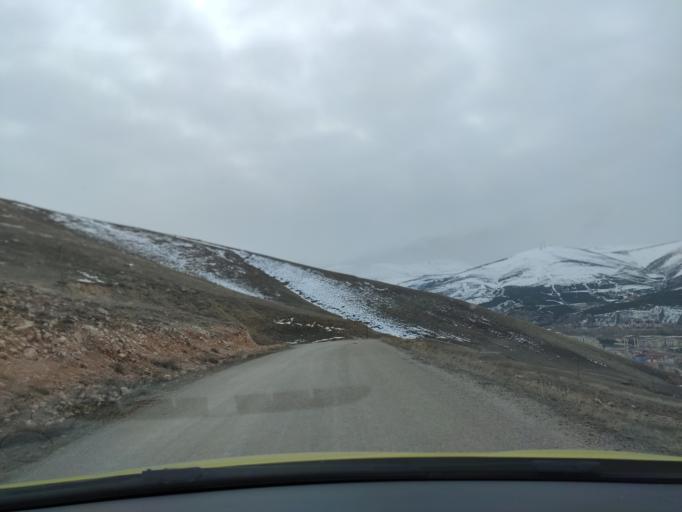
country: TR
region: Bayburt
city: Bayburt
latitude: 40.2585
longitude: 40.2410
